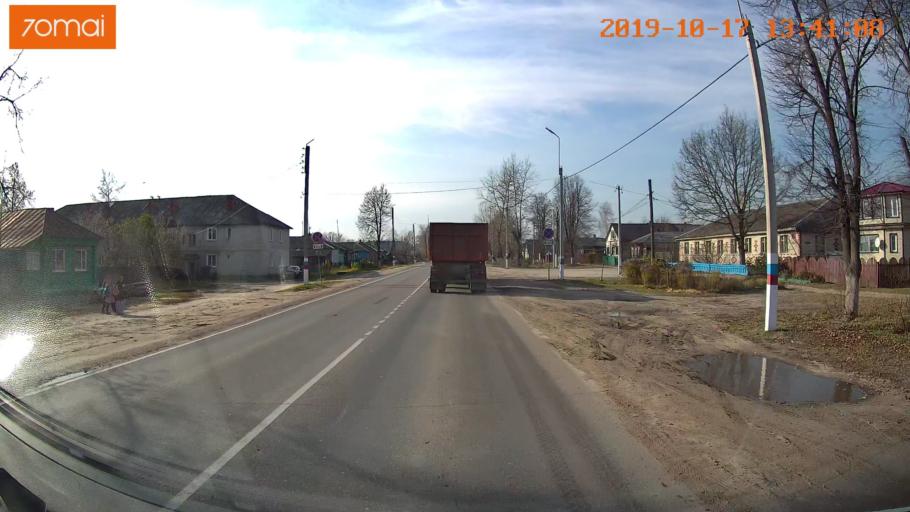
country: RU
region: Rjazan
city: Tuma
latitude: 55.1490
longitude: 40.5679
